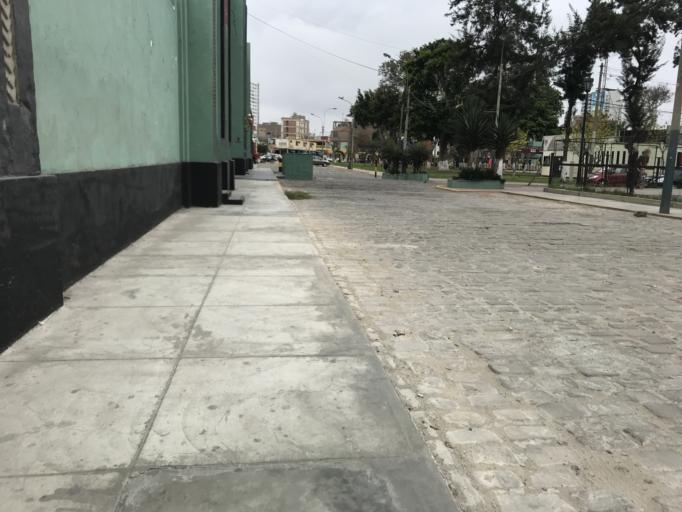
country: PE
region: Lima
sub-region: Lima
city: San Isidro
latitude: -12.0779
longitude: -77.0606
